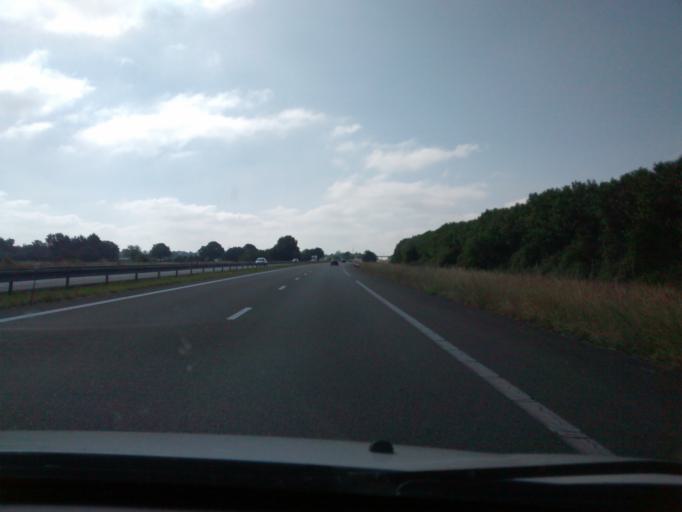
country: FR
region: Pays de la Loire
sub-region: Departement de la Mayenne
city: Bonchamp-les-Laval
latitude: 48.0932
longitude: -0.6861
